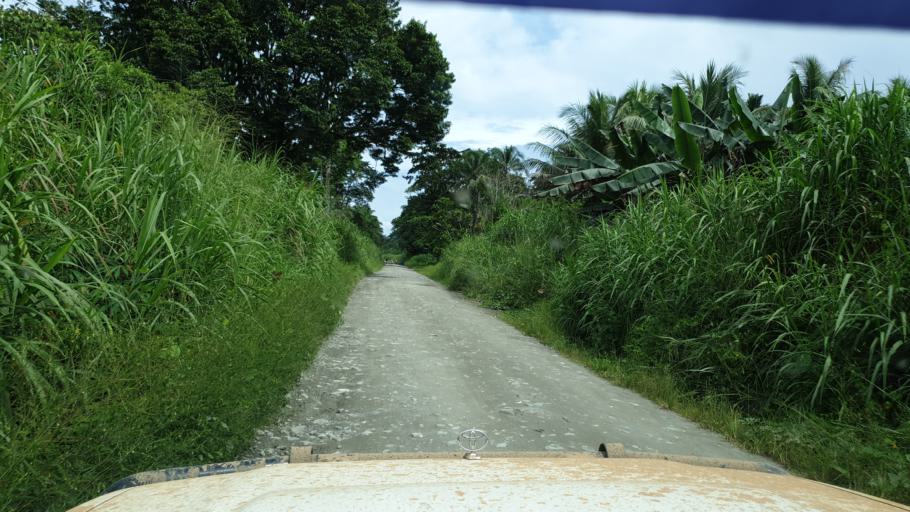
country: PG
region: Northern Province
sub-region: Sohe
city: Kokoda
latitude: -8.8948
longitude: 147.7498
